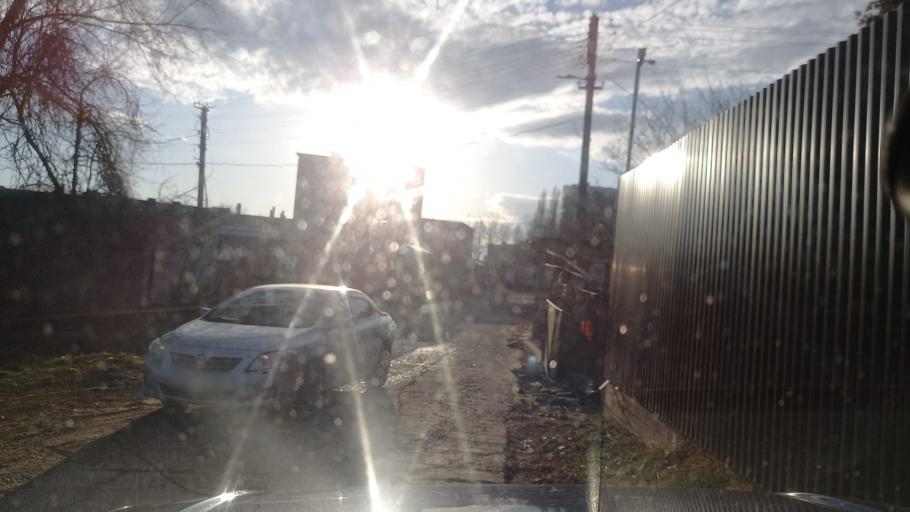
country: RU
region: Krasnodarskiy
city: Pashkovskiy
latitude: 45.0123
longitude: 39.1061
